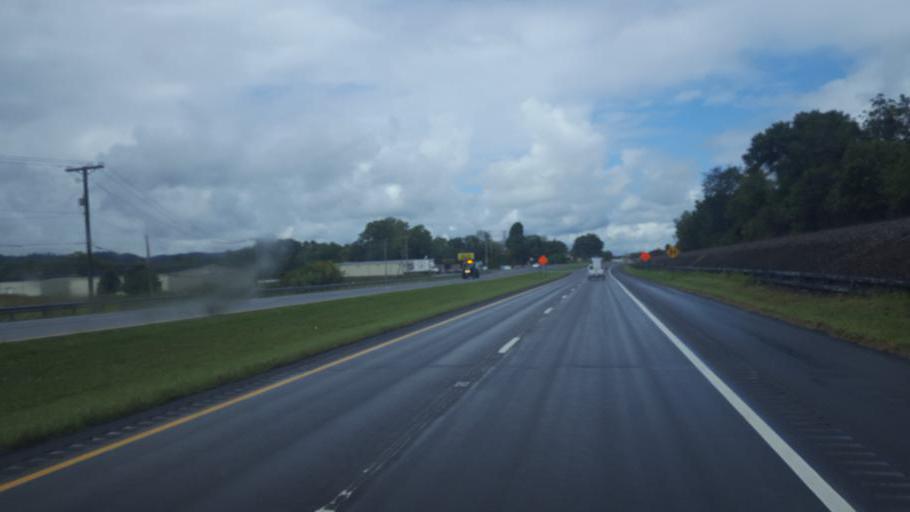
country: US
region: Ohio
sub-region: Scioto County
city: Lucasville
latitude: 38.8707
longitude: -82.9942
